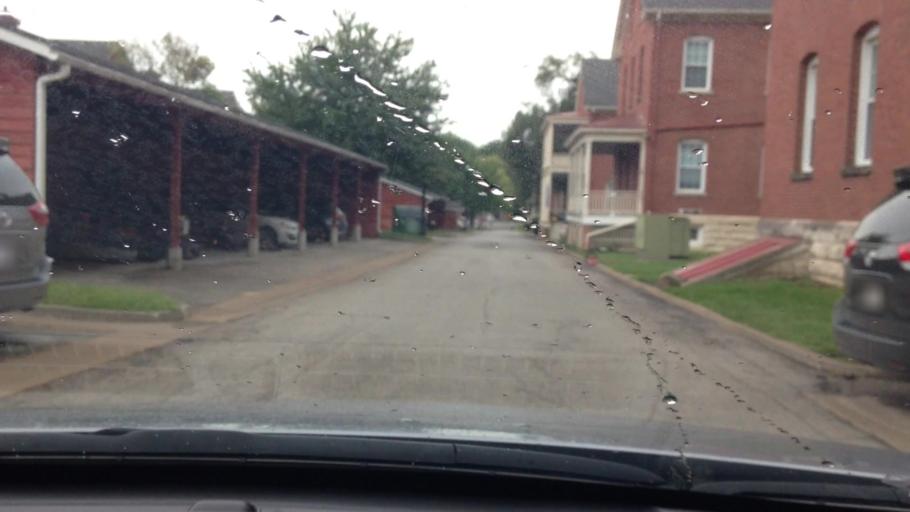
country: US
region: Kansas
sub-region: Leavenworth County
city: Leavenworth
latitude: 39.3519
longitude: -94.9213
